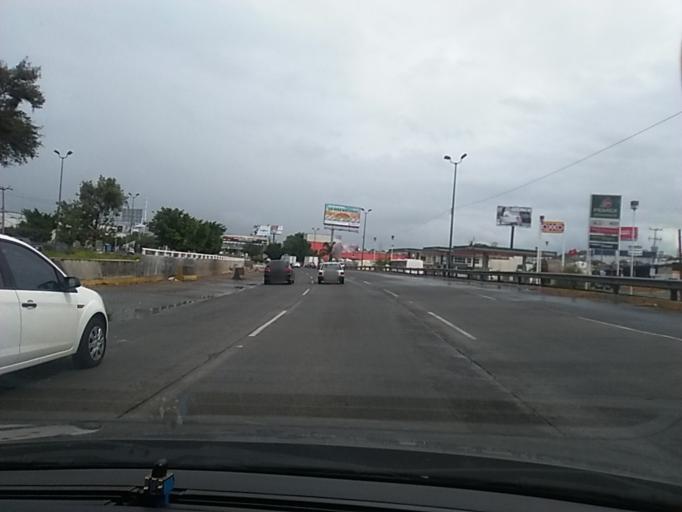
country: MX
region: Jalisco
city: Tlaquepaque
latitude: 20.6250
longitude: -103.3277
